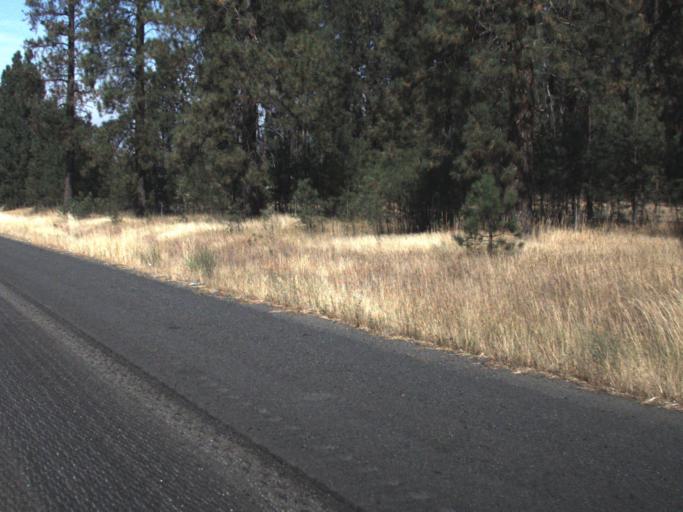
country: US
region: Washington
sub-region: Spokane County
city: Mead
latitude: 47.8135
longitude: -117.3469
